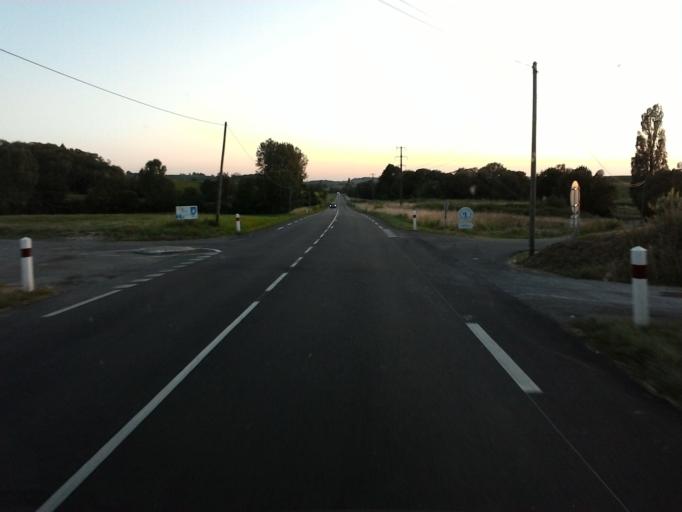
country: FR
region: Franche-Comte
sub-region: Departement du Jura
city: Arbois
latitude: 46.8999
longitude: 5.7496
